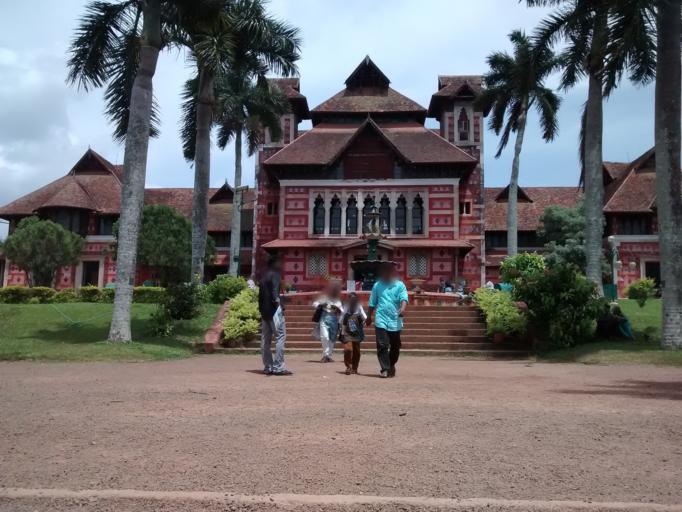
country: IN
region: Kerala
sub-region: Thiruvananthapuram
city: Thiruvananthapuram
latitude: 8.5093
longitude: 76.9548
